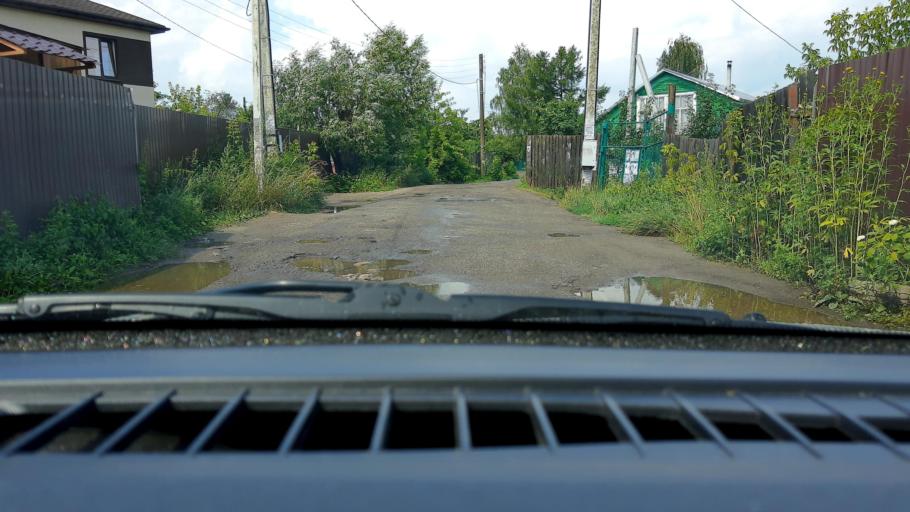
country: RU
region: Nizjnij Novgorod
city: Gorbatovka
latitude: 56.3814
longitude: 43.8277
